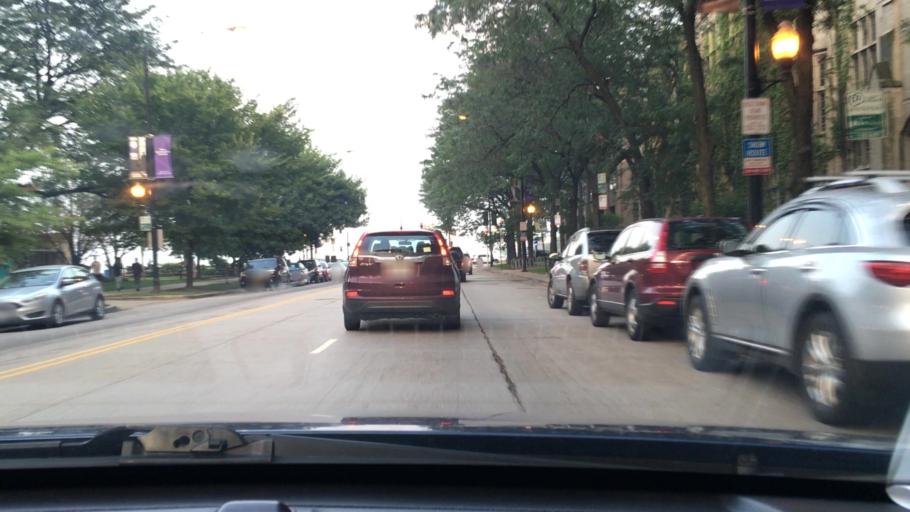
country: US
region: Illinois
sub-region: Cook County
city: Chicago
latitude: 41.8968
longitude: -87.6186
